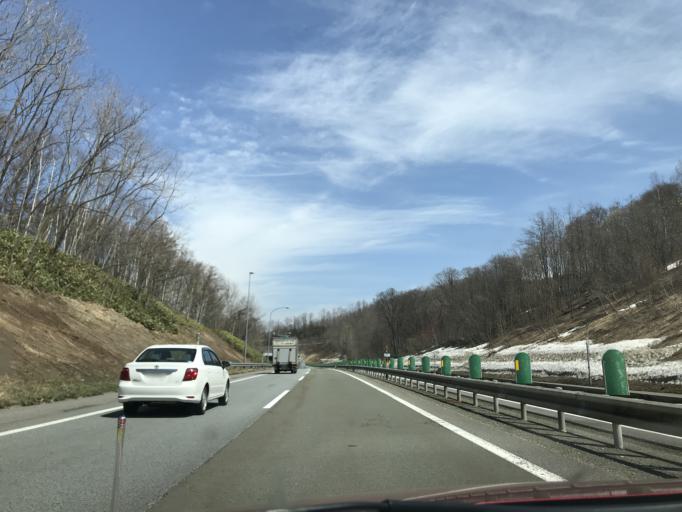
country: JP
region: Hokkaido
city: Bibai
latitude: 43.2850
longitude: 141.8593
